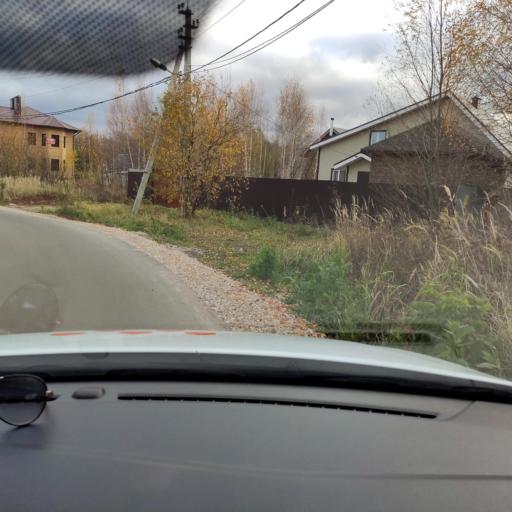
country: RU
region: Tatarstan
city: Stolbishchi
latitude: 55.7358
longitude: 49.2680
